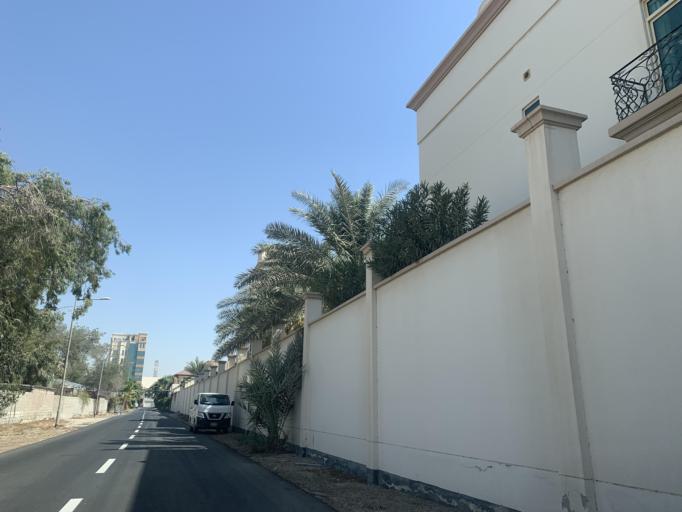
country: BH
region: Manama
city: Jidd Hafs
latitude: 26.2244
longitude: 50.5010
